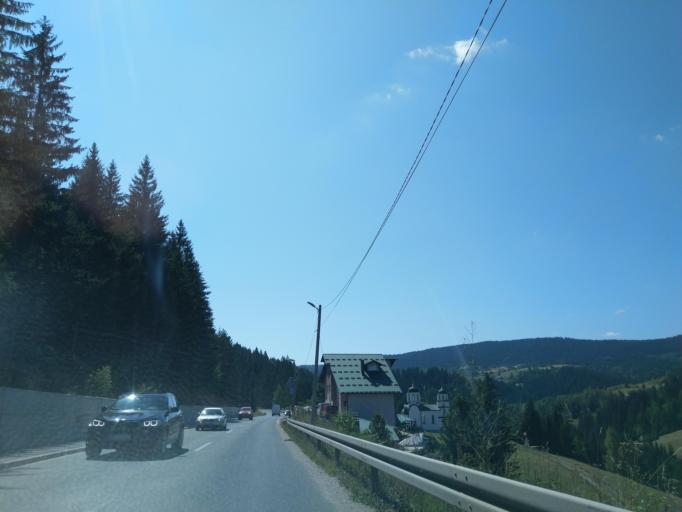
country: RS
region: Central Serbia
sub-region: Zlatiborski Okrug
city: Nova Varos
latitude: 43.4398
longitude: 19.8216
